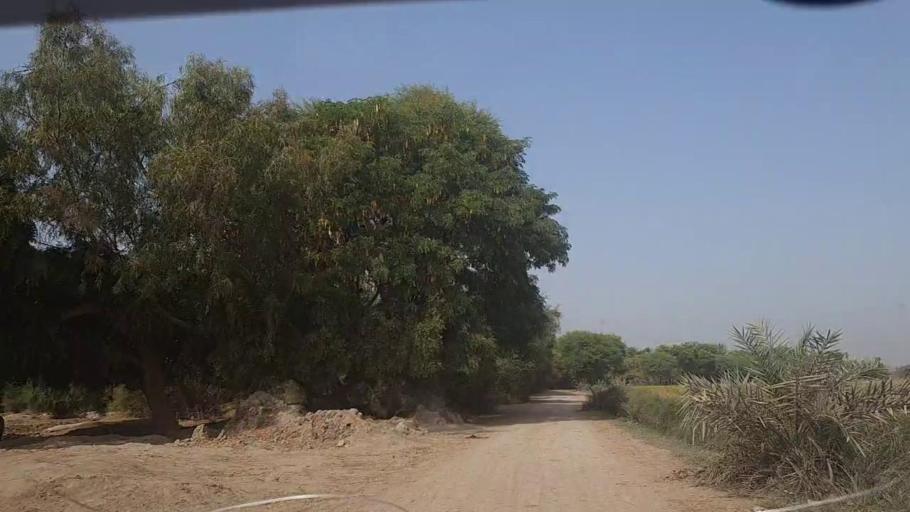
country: PK
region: Sindh
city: Madeji
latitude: 27.7983
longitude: 68.4247
